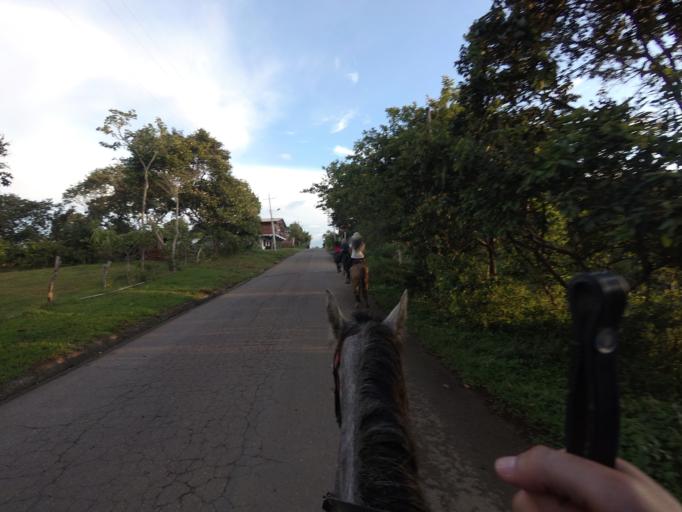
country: CO
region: Huila
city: San Agustin
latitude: 1.8926
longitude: -76.2725
